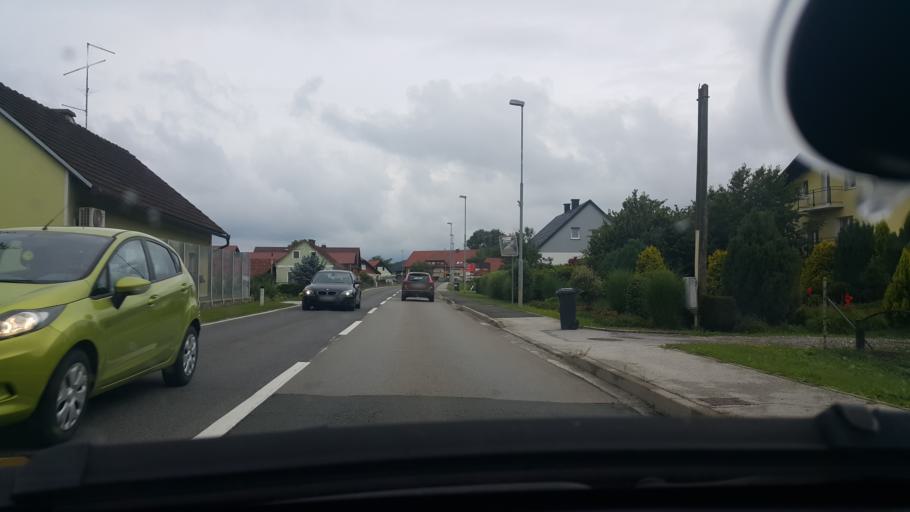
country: SI
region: Ormoz
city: Ormoz
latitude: 46.4151
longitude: 16.1128
